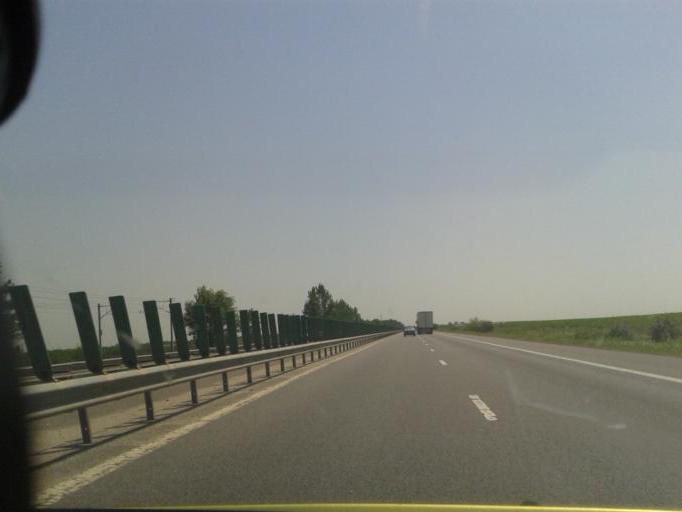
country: RO
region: Calarasi
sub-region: Comuna Nicolae Balcescu
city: Nicolae Balcescu
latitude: 44.4467
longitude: 26.7216
